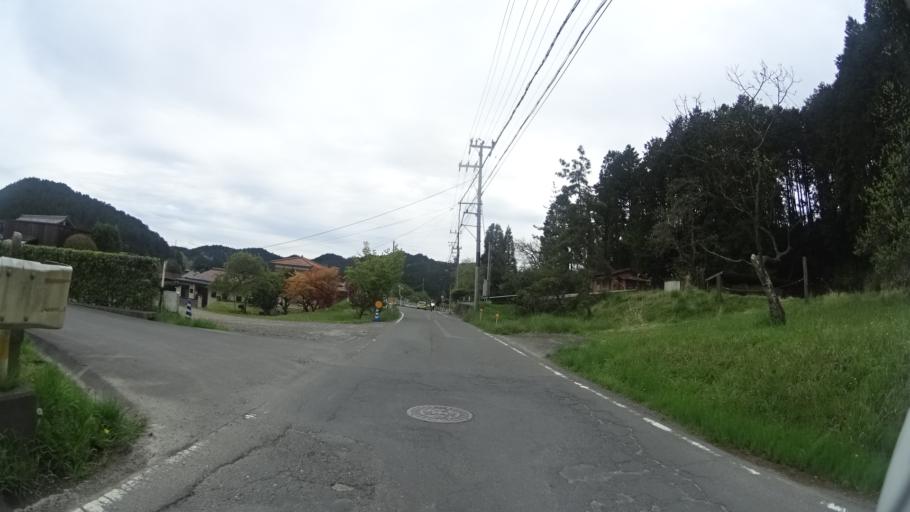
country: JP
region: Kyoto
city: Kameoka
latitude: 35.1943
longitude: 135.4624
